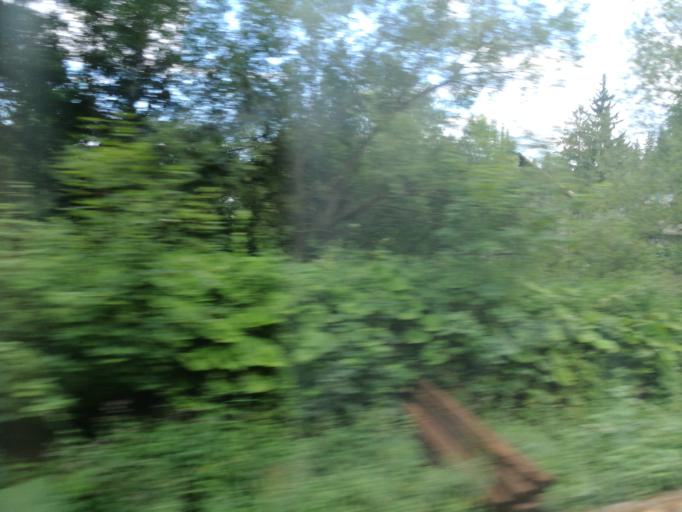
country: RO
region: Brasov
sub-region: Oras Predeal
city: Predeal
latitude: 45.5333
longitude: 25.5793
